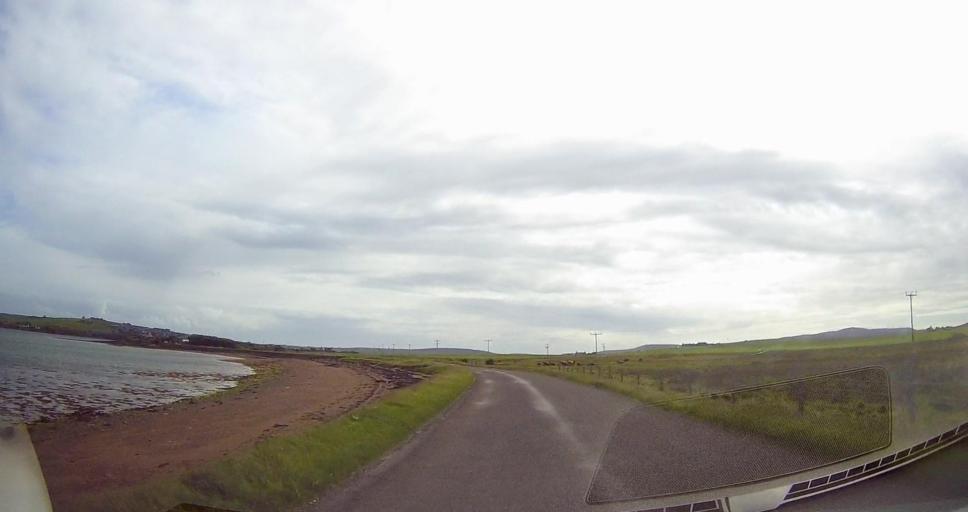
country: GB
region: Scotland
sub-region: Orkney Islands
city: Stromness
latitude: 58.8110
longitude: -3.2014
